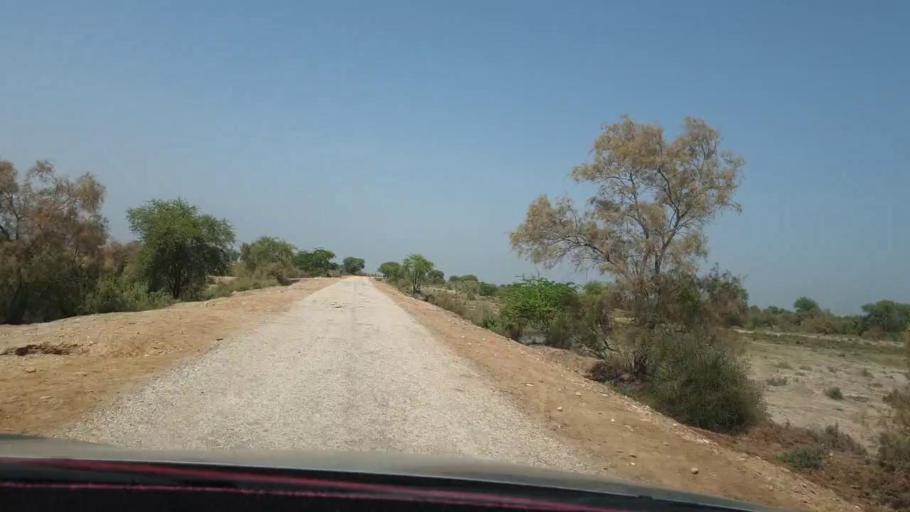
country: PK
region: Sindh
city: Warah
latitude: 27.5079
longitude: 67.7046
